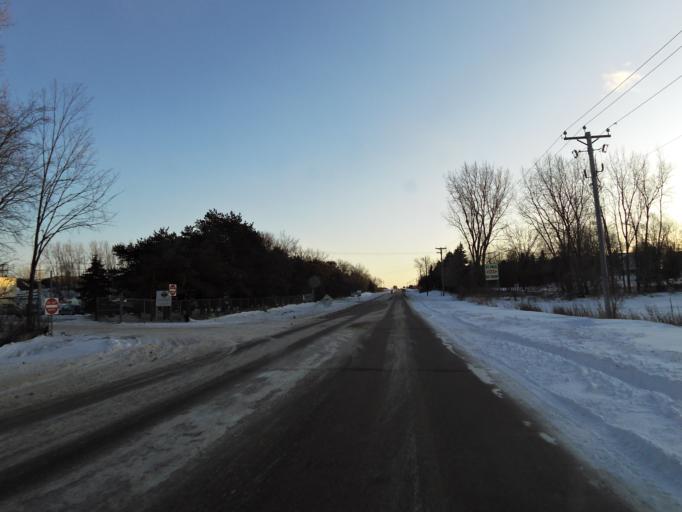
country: US
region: Minnesota
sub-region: Washington County
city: Lake Elmo
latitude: 44.9425
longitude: -92.8831
